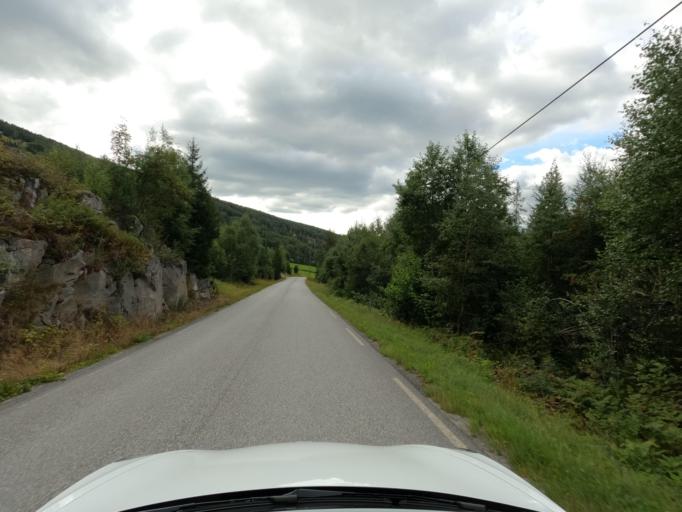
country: NO
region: Buskerud
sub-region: Nore og Uvdal
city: Rodberg
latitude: 60.0199
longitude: 8.8358
